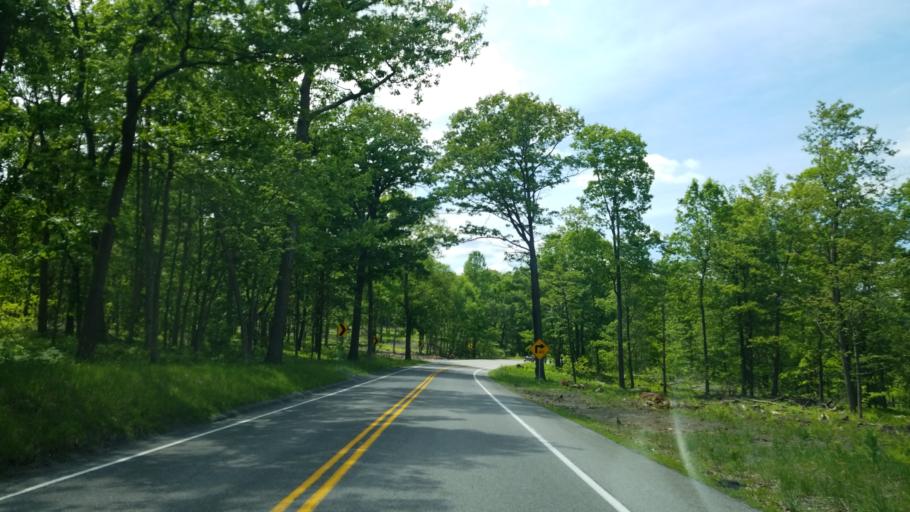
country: US
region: Pennsylvania
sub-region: Blair County
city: Tipton
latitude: 40.7016
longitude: -78.3040
